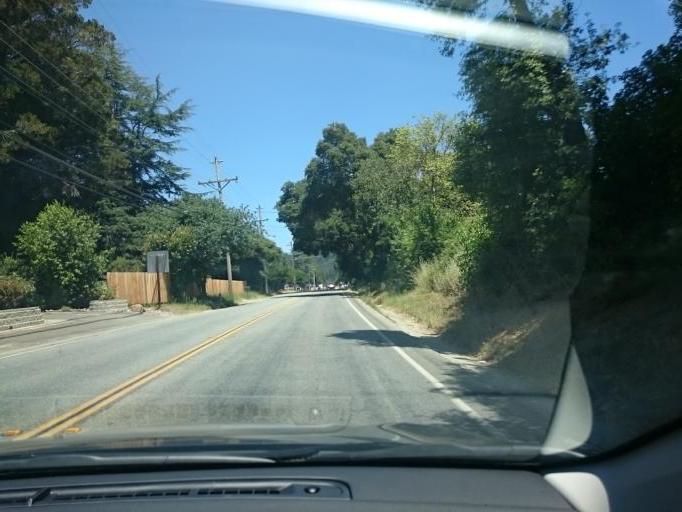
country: US
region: California
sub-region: Santa Cruz County
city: Felton
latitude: 37.0454
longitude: -122.0734
